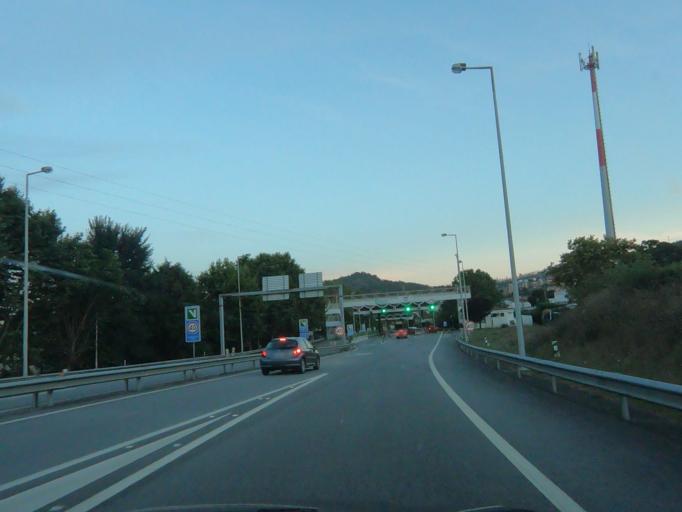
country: PT
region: Porto
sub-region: Valongo
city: Valongo
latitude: 41.1959
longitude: -8.5050
